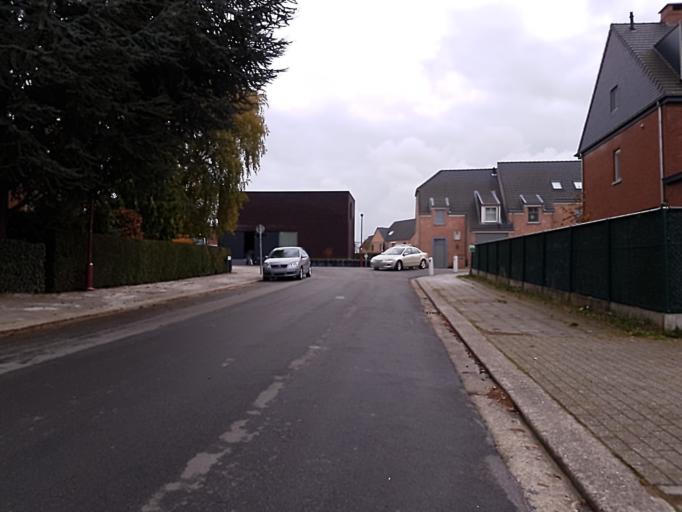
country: BE
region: Flanders
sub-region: Provincie Antwerpen
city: Lint
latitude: 51.1346
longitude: 4.4870
